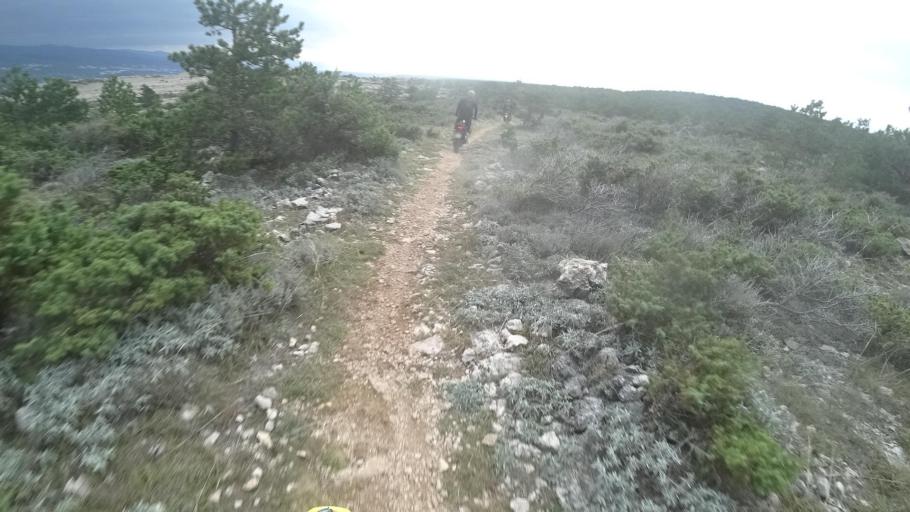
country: HR
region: Primorsko-Goranska
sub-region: Grad Crikvenica
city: Jadranovo
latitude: 45.2136
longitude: 14.5907
